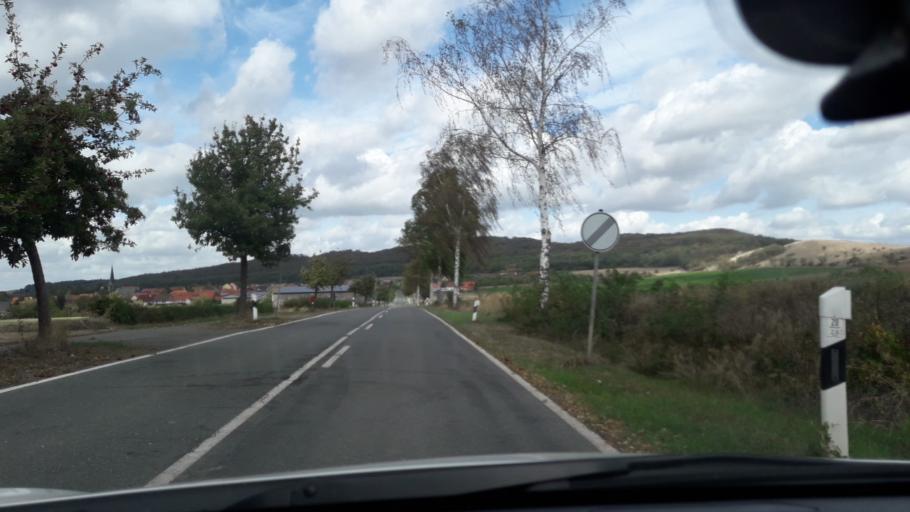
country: DE
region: Lower Saxony
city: Liebenburg
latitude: 52.0006
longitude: 10.3980
